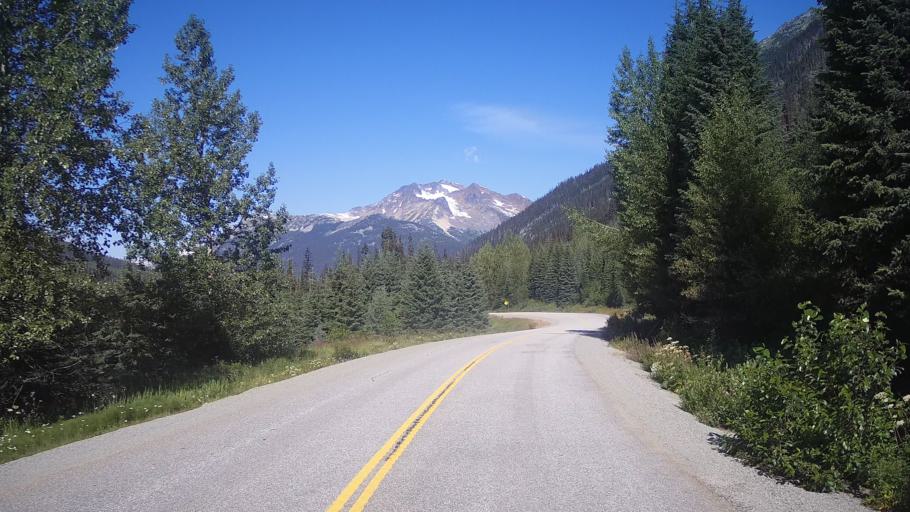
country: CA
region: British Columbia
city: Pemberton
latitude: 50.3811
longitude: -122.4095
